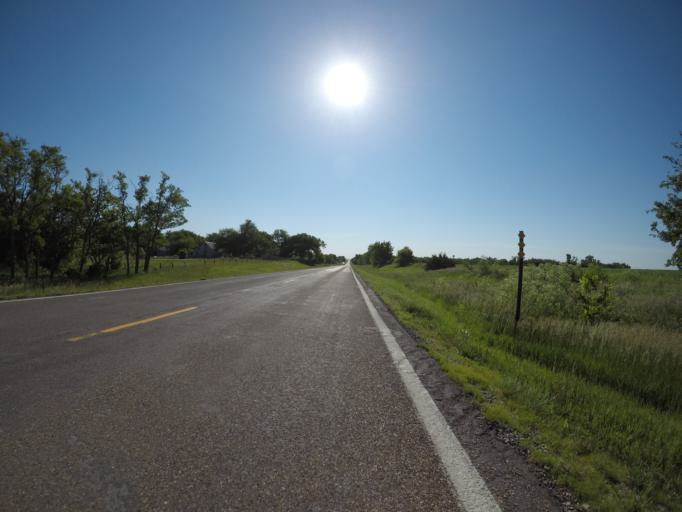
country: US
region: Kansas
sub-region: Lyon County
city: Emporia
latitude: 38.6587
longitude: -96.1811
